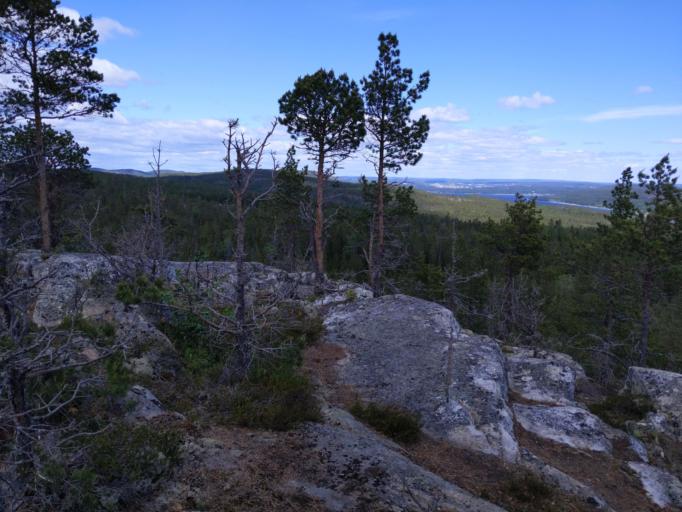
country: SE
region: Vaesternorrland
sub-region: OErnskoeldsviks Kommun
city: Kopmanholmen
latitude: 63.1770
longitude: 18.6828
